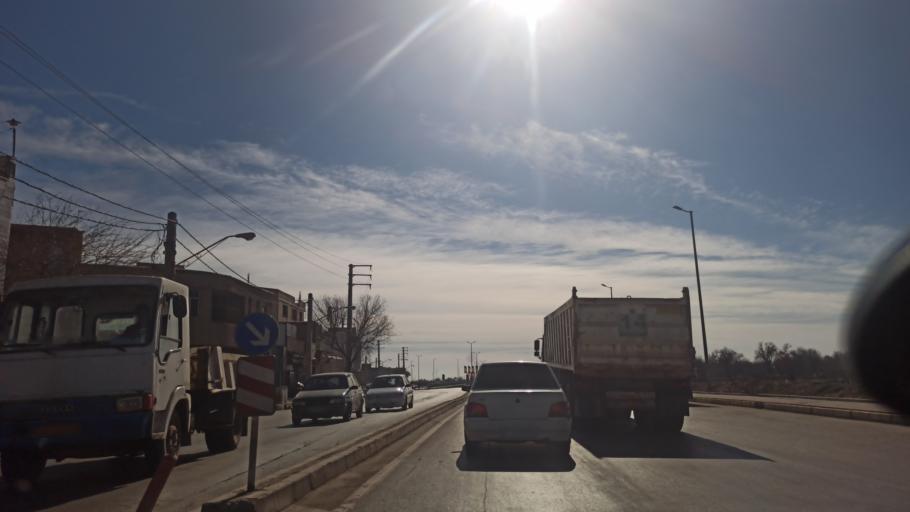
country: IR
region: Qazvin
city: Qazvin
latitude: 36.2486
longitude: 50.0020
